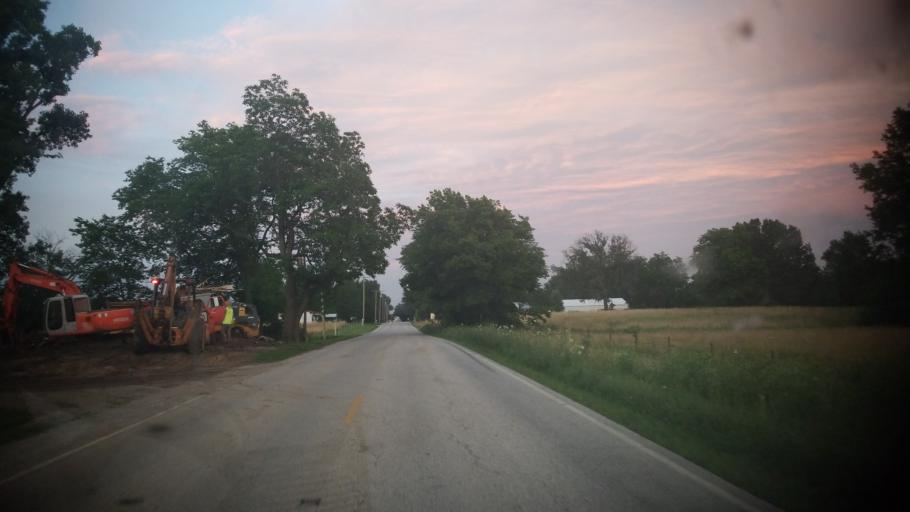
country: US
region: Illinois
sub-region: Clay County
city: Flora
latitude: 38.5158
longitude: -88.4447
